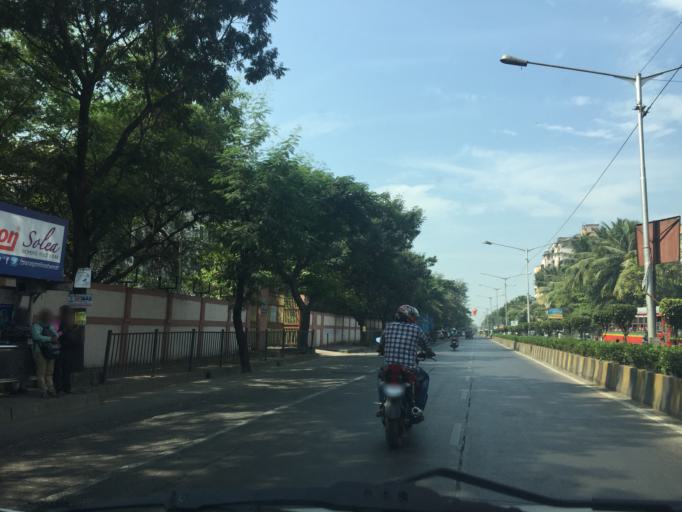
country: IN
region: Maharashtra
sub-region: Mumbai Suburban
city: Borivli
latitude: 19.2321
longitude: 72.8305
